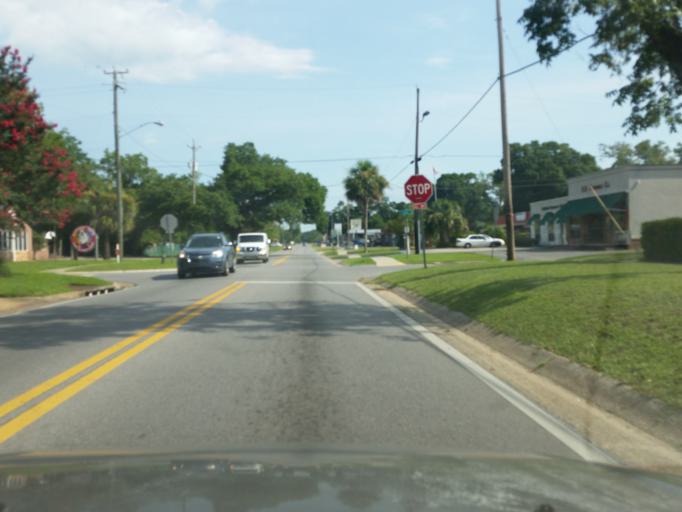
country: US
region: Florida
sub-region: Escambia County
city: Goulding
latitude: 30.4416
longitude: -87.2066
